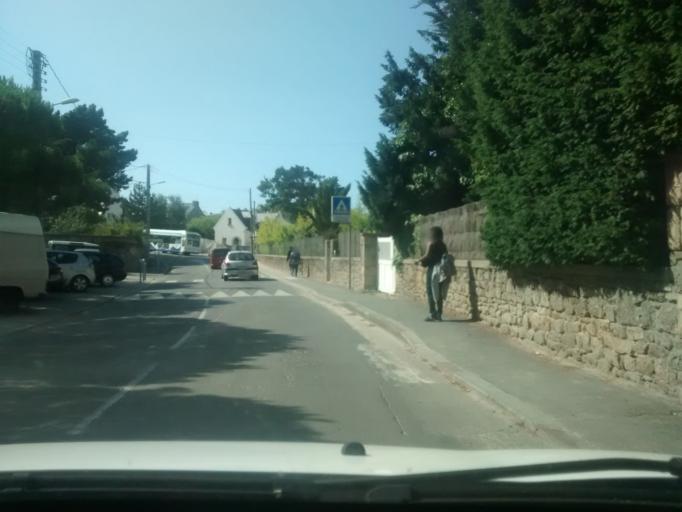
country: FR
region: Brittany
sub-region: Departement d'Ille-et-Vilaine
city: Saint-Coulomb
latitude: 48.6810
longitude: -1.9632
